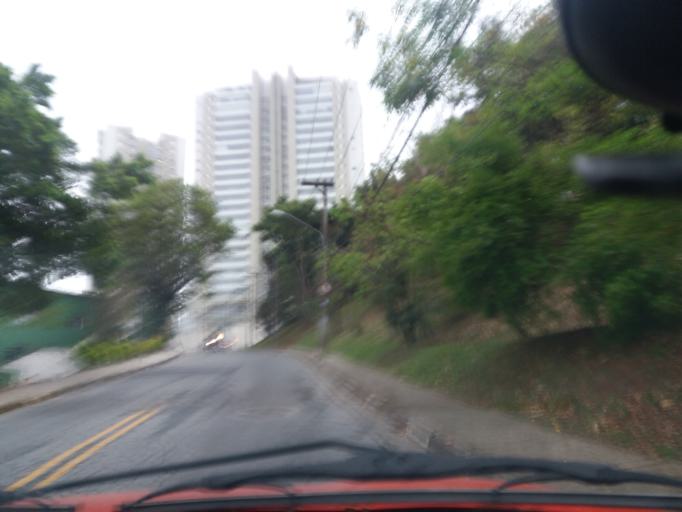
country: BR
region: Sao Paulo
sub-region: Taboao Da Serra
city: Taboao da Serra
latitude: -23.5906
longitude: -46.7410
